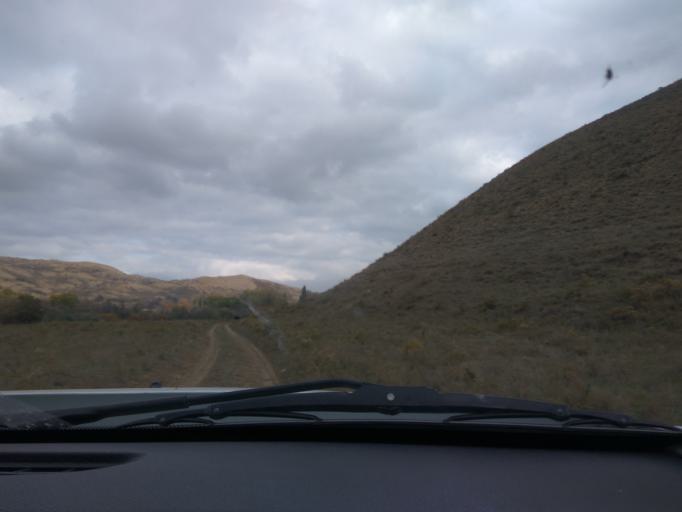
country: RU
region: Dagestan
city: Korkmaskala
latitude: 42.9970
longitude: 47.2334
